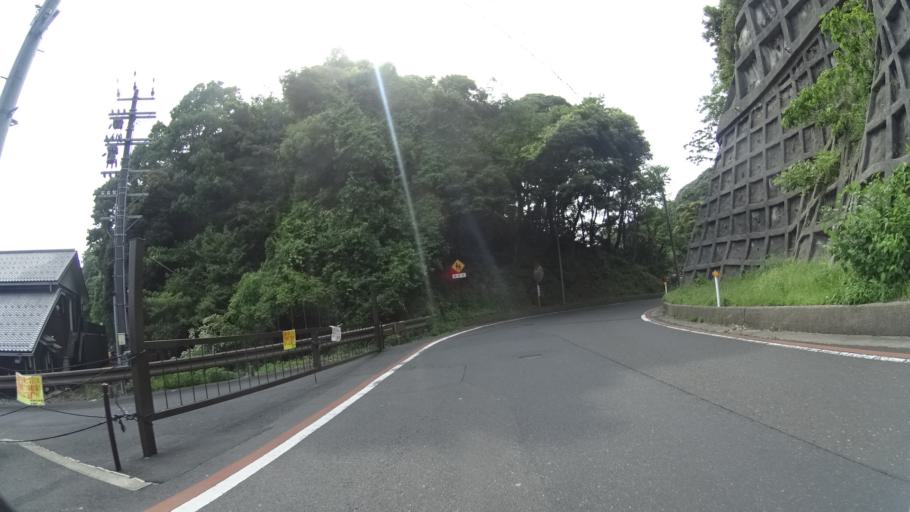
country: JP
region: Kyoto
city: Miyazu
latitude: 35.6685
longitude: 135.2806
